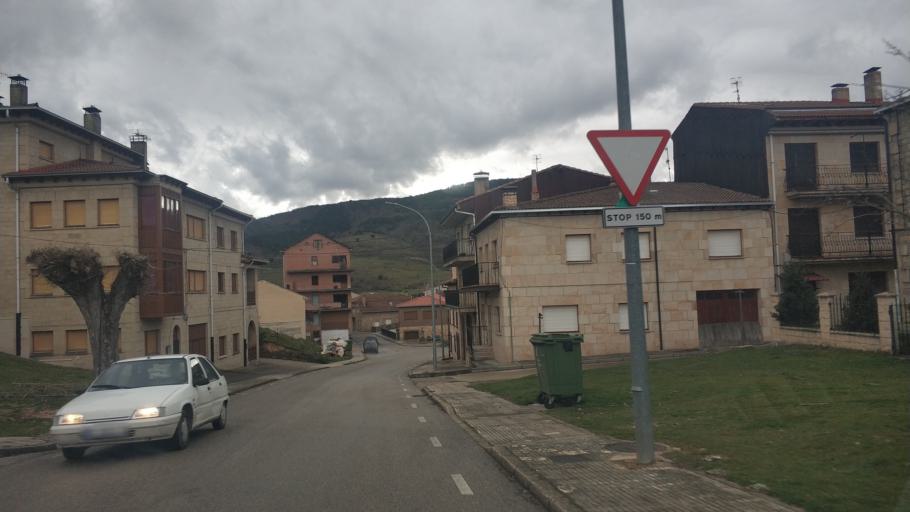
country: ES
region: Castille and Leon
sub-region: Provincia de Burgos
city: Canicosa de la Sierra
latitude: 41.9376
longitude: -3.0397
